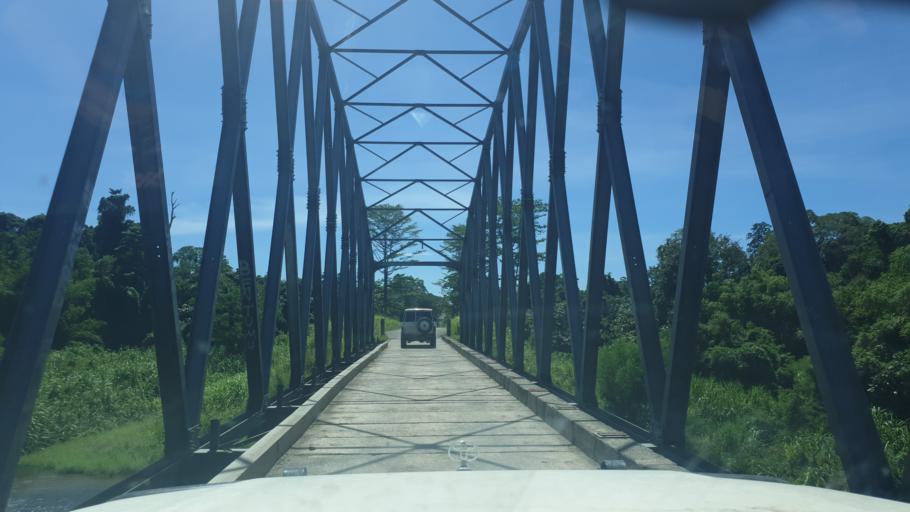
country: PG
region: Bougainville
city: Arawa
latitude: -5.8184
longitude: 155.1476
